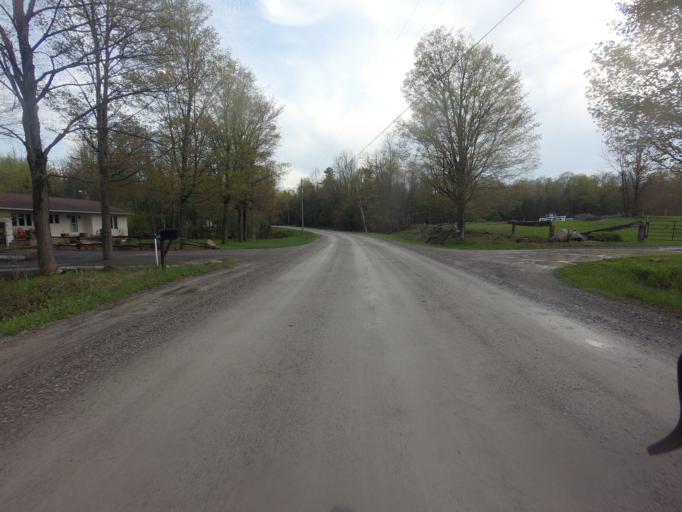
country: CA
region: Ontario
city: Carleton Place
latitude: 45.1998
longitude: -76.3262
